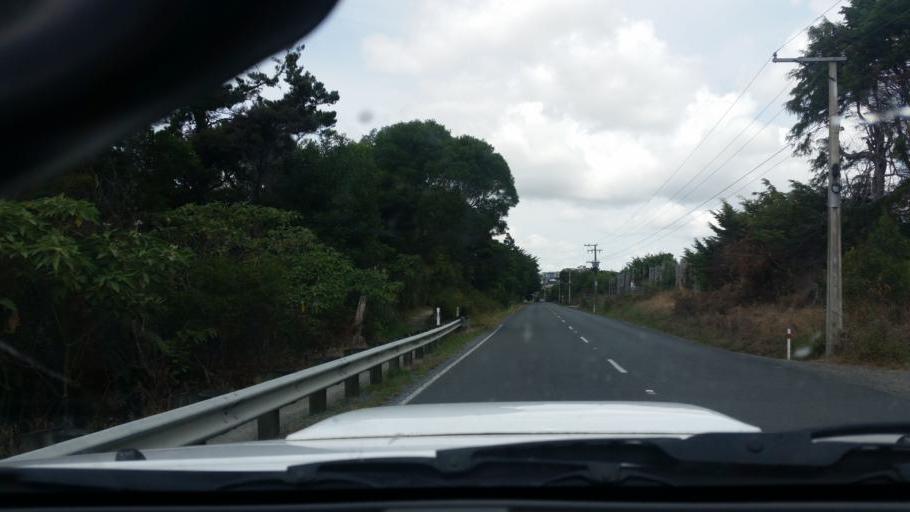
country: NZ
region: Auckland
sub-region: Auckland
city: Wellsford
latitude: -36.1189
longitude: 174.5730
